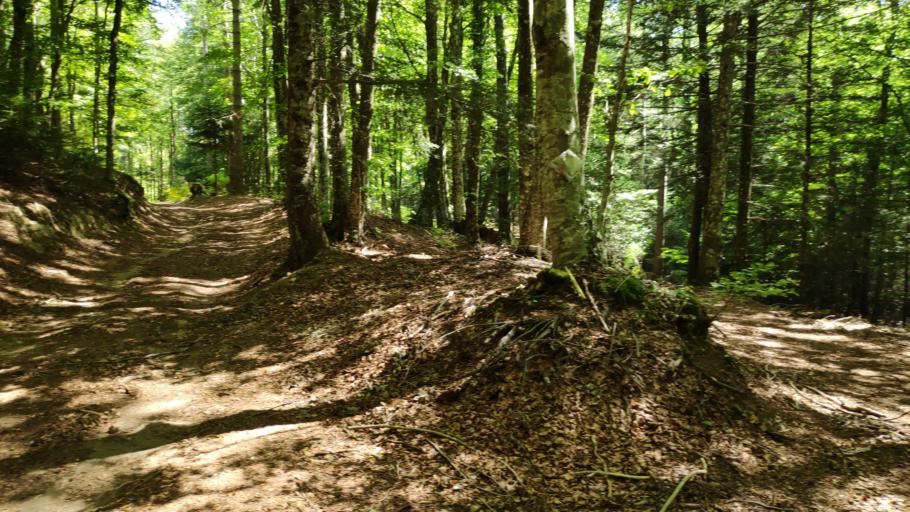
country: IT
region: Calabria
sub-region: Provincia di Vibo-Valentia
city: Mongiana
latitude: 38.5275
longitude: 16.3822
